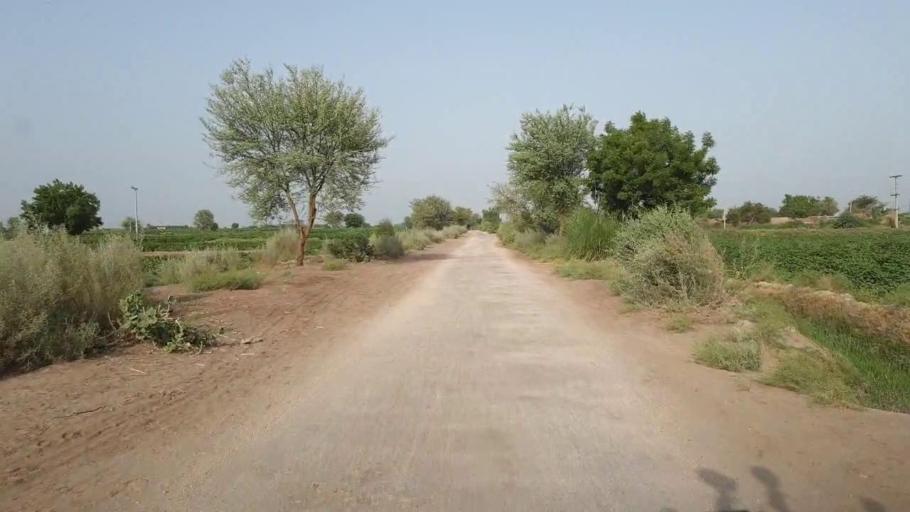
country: PK
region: Sindh
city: Daur
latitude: 26.3431
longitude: 68.2725
